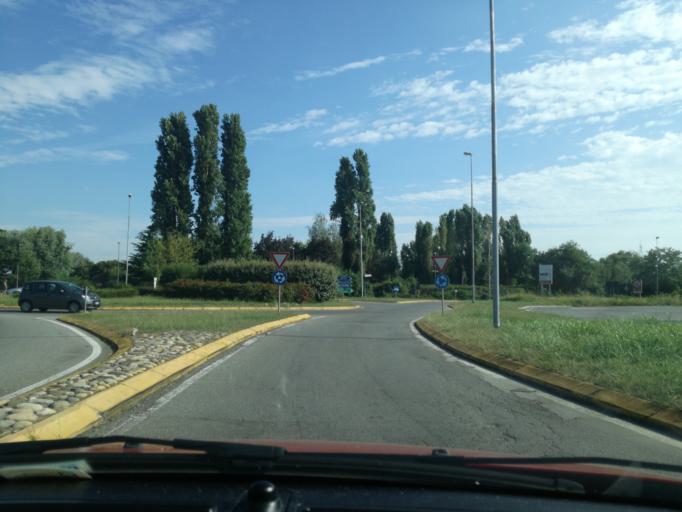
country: IT
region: Lombardy
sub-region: Provincia di Monza e Brianza
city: Velasca
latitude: 45.6426
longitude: 9.3459
